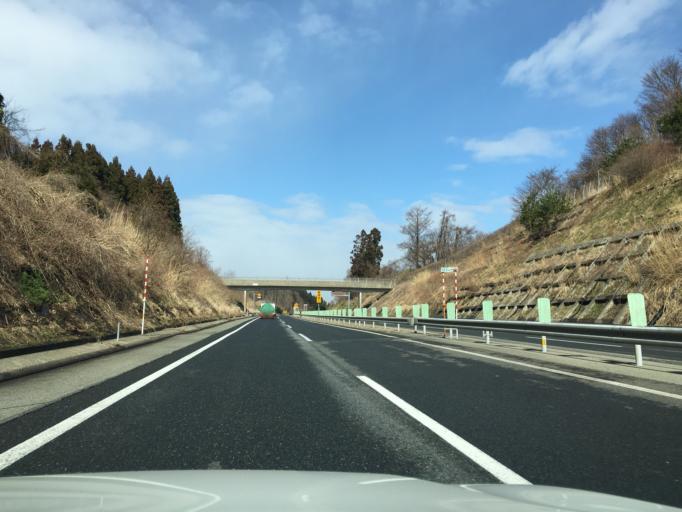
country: JP
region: Akita
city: Akita Shi
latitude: 39.7846
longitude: 140.1093
